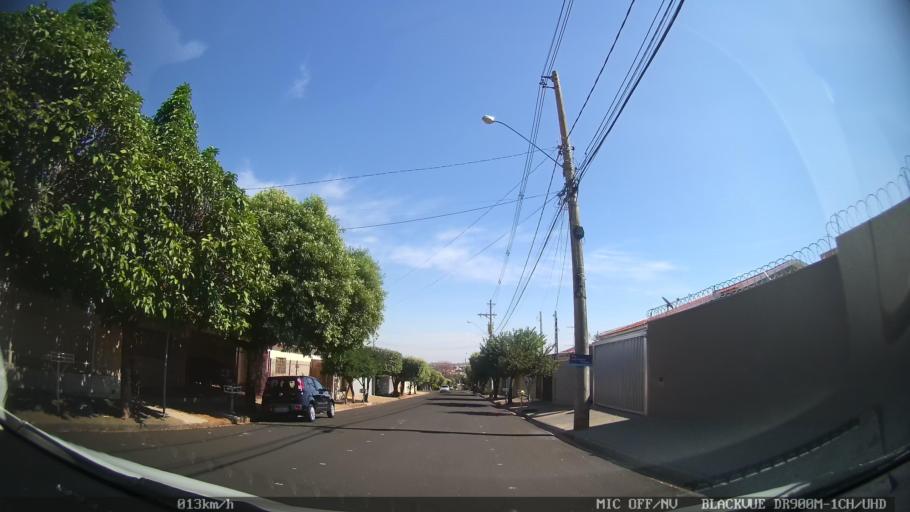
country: BR
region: Sao Paulo
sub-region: Sao Jose Do Rio Preto
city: Sao Jose do Rio Preto
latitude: -20.7821
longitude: -49.3741
